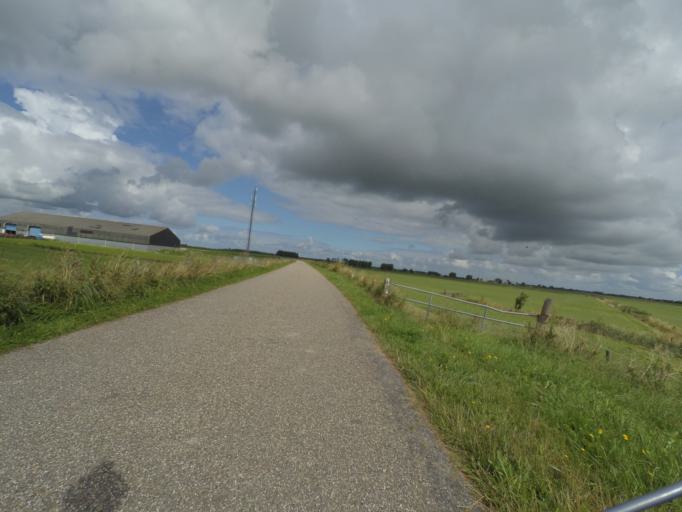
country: NL
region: Groningen
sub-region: Gemeente Zuidhorn
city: Grijpskerk
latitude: 53.3080
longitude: 6.2655
